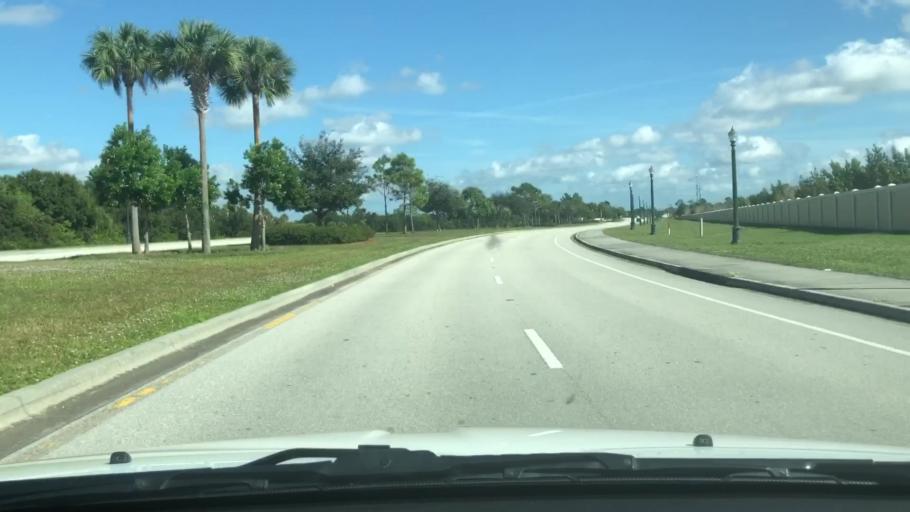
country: US
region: Florida
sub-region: Saint Lucie County
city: Port Saint Lucie
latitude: 27.2944
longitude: -80.4322
